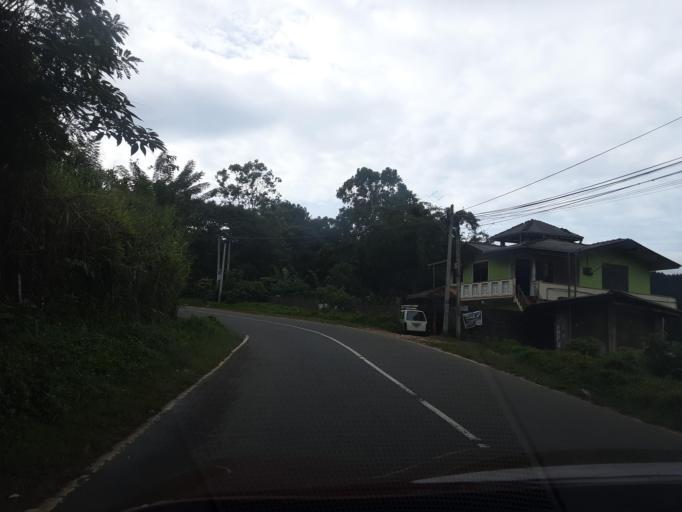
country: LK
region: Uva
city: Haputale
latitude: 6.8498
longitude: 80.9689
